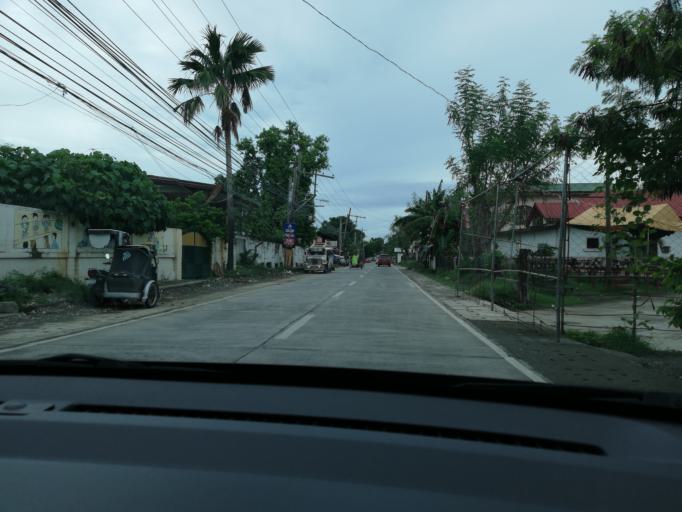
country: PH
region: Ilocos
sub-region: Province of Ilocos Sur
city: Bantay
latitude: 17.5830
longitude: 120.3853
